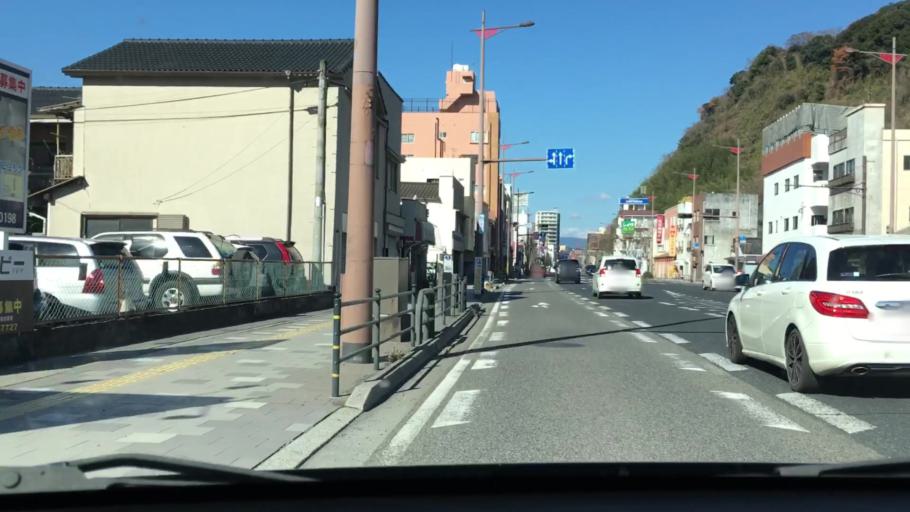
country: JP
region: Kagoshima
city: Kagoshima-shi
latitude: 31.5942
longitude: 130.5432
